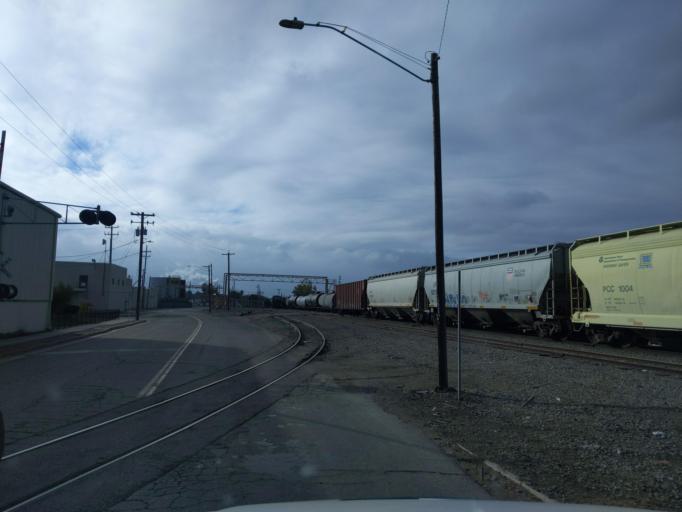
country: US
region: California
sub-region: San Joaquin County
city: Stockton
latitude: 37.9476
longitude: -121.3078
